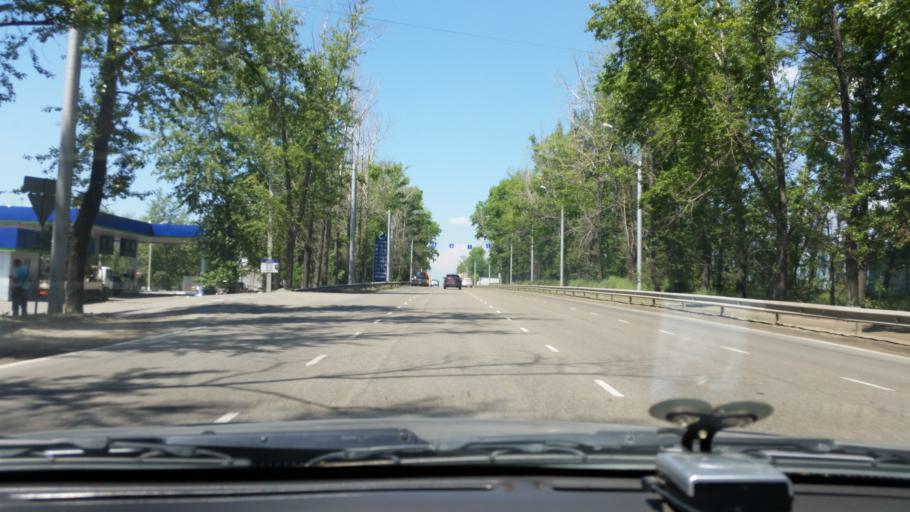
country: RU
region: Irkutsk
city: Dzerzhinsk
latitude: 52.2624
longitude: 104.3519
